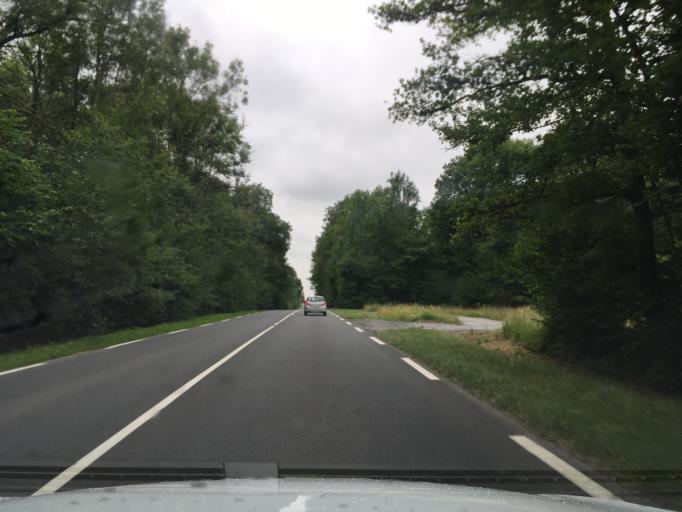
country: FR
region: Picardie
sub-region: Departement de l'Aisne
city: Buironfosse
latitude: 49.9706
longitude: 3.8679
